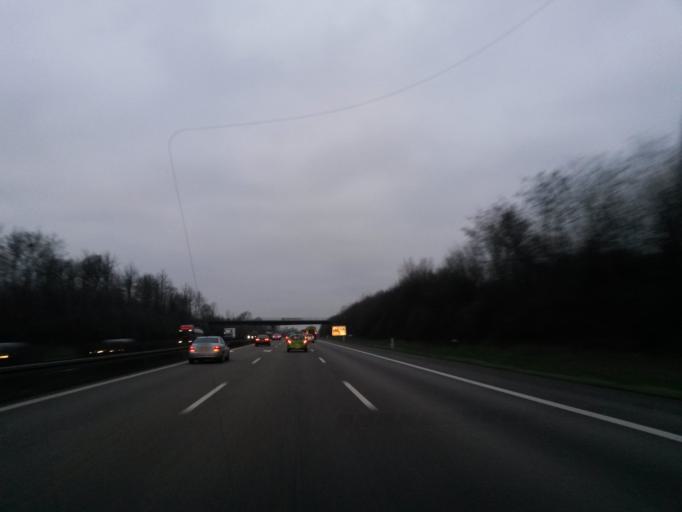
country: DE
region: Baden-Wuerttemberg
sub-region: Regierungsbezirk Stuttgart
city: Mundelsheim
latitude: 48.9807
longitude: 9.2299
